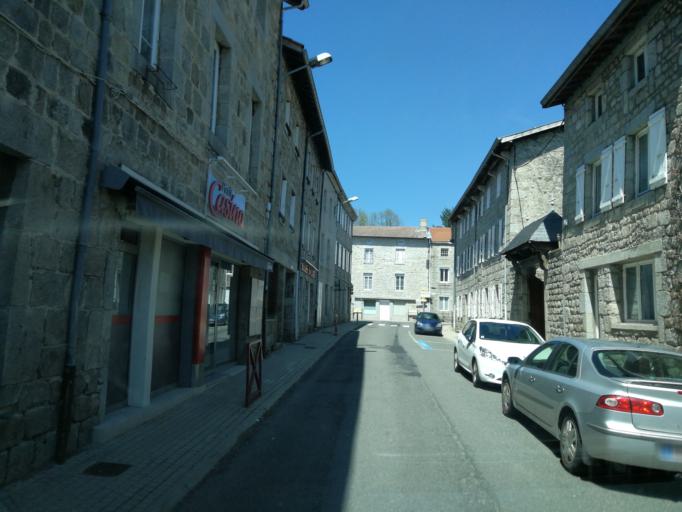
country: FR
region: Rhone-Alpes
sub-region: Departement de la Loire
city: Marlhes
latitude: 45.2833
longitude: 4.3945
